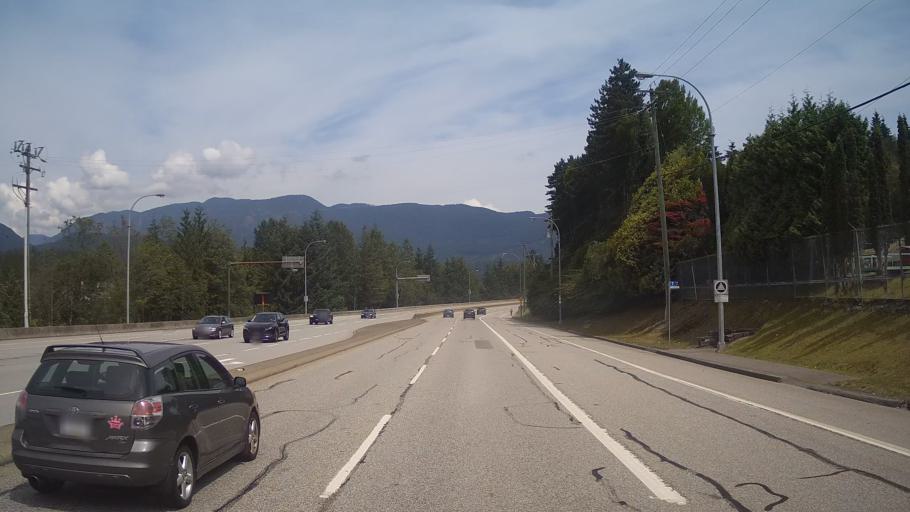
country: CA
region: British Columbia
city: Port Moody
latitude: 49.2884
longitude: -122.8967
